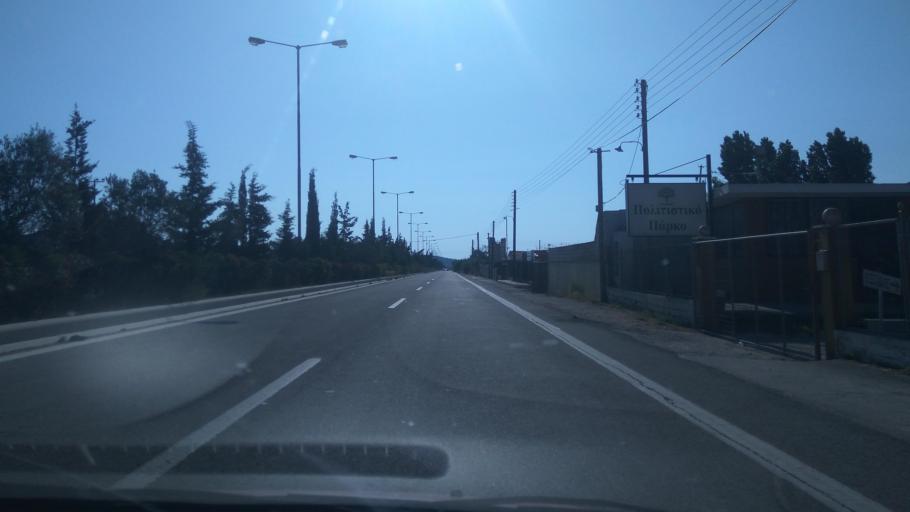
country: GR
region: Attica
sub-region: Nomarchia Anatolikis Attikis
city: Keratea
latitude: 37.8017
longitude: 24.0173
